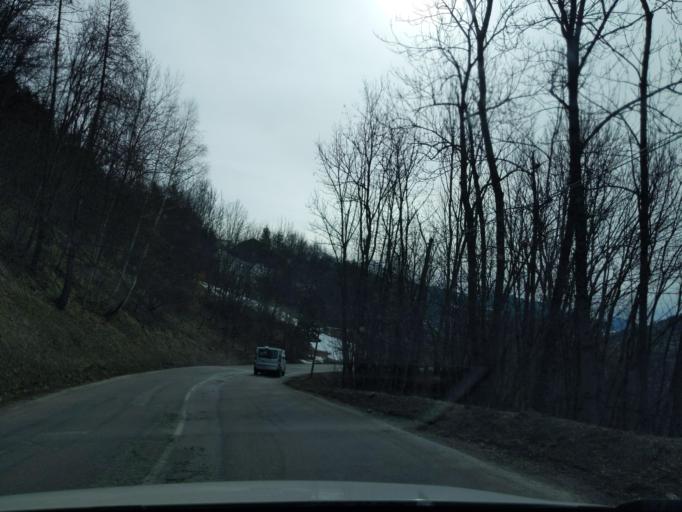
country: FR
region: Rhone-Alpes
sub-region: Departement de la Savoie
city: Bourg-Saint-Maurice
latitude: 45.6048
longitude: 6.7772
